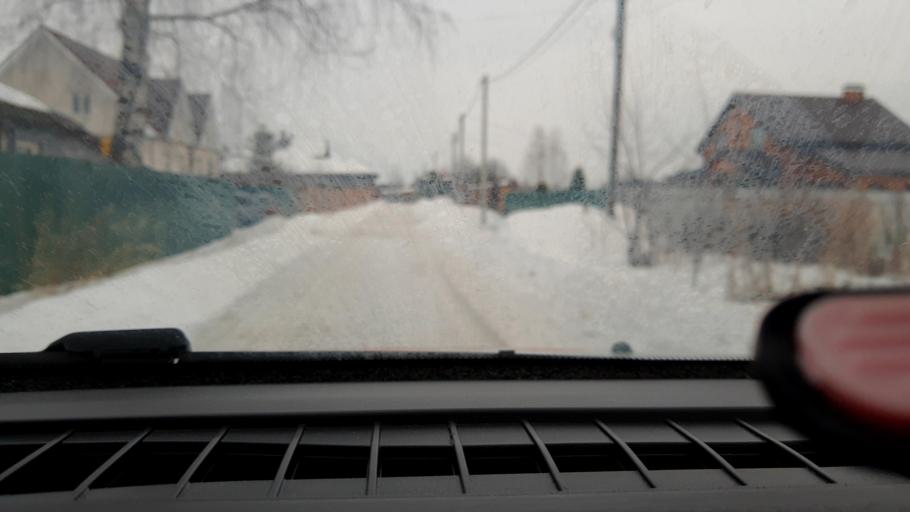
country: RU
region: Nizjnij Novgorod
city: Lukino
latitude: 56.4159
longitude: 43.6904
